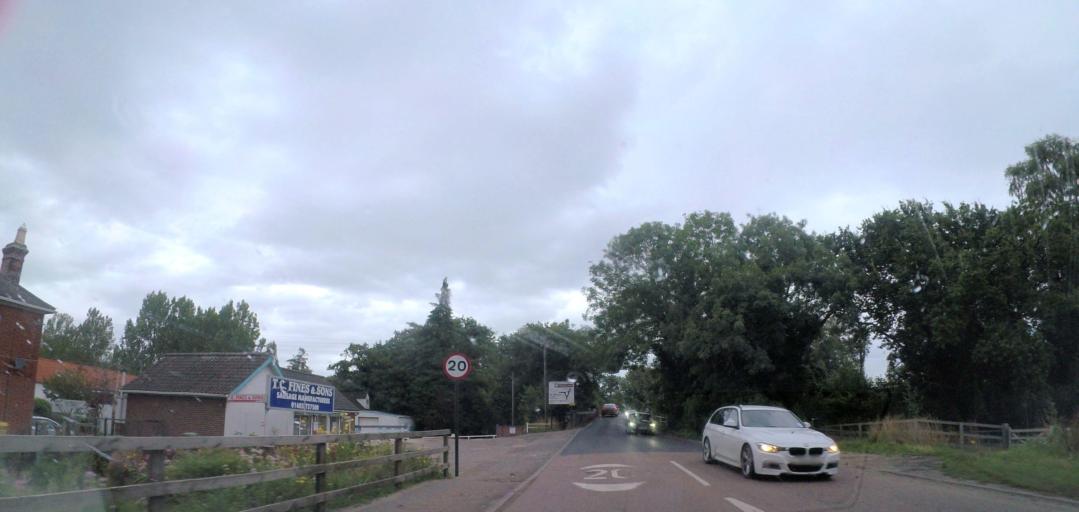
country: GB
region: England
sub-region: Norfolk
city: Coltishall
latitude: 52.7279
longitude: 1.3548
